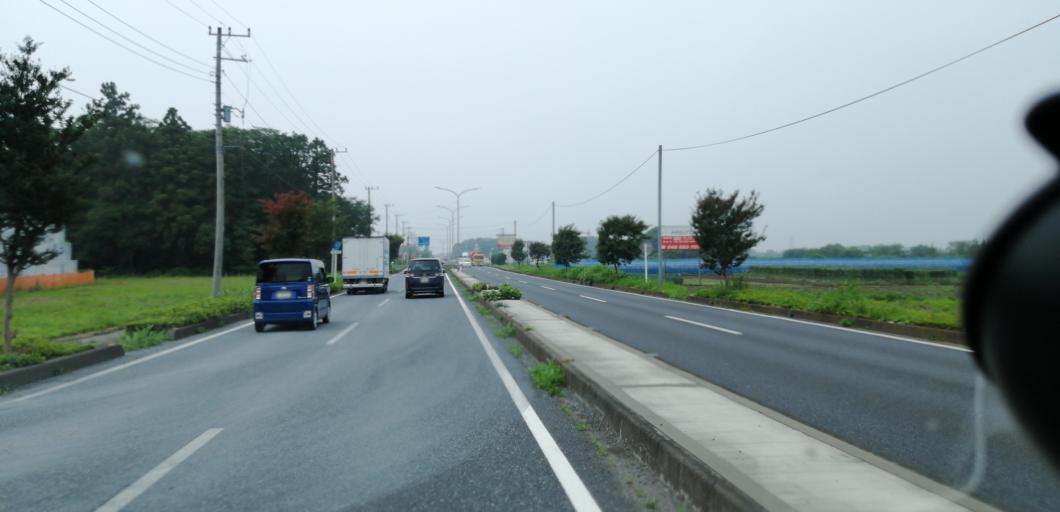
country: JP
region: Saitama
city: Fukayacho
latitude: 36.1473
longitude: 139.2690
